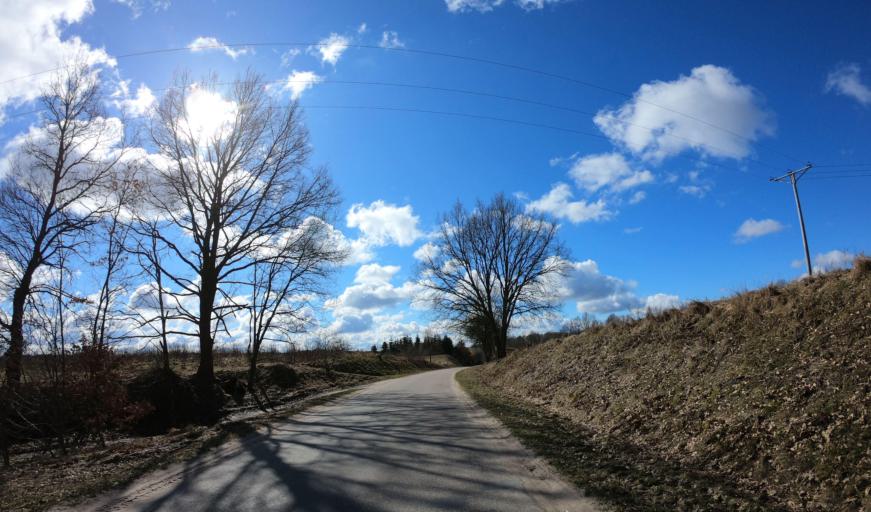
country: PL
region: West Pomeranian Voivodeship
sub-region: Powiat drawski
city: Zlocieniec
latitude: 53.4795
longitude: 15.9811
